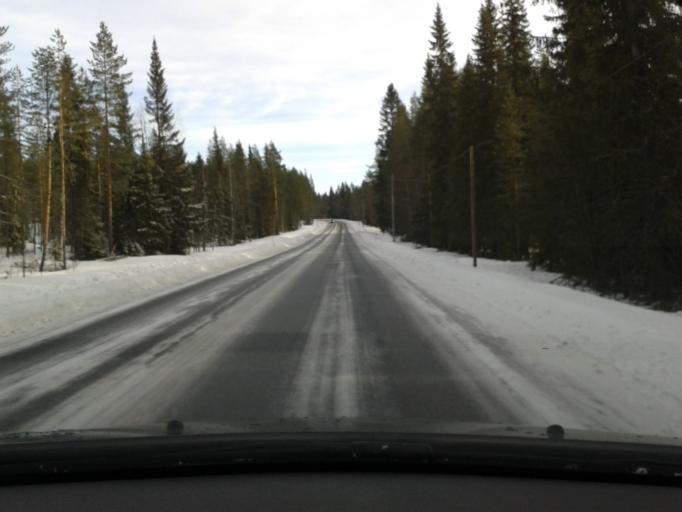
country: SE
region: Vaesterbotten
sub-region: Vilhelmina Kommun
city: Vilhelmina
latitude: 64.6475
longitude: 16.5231
